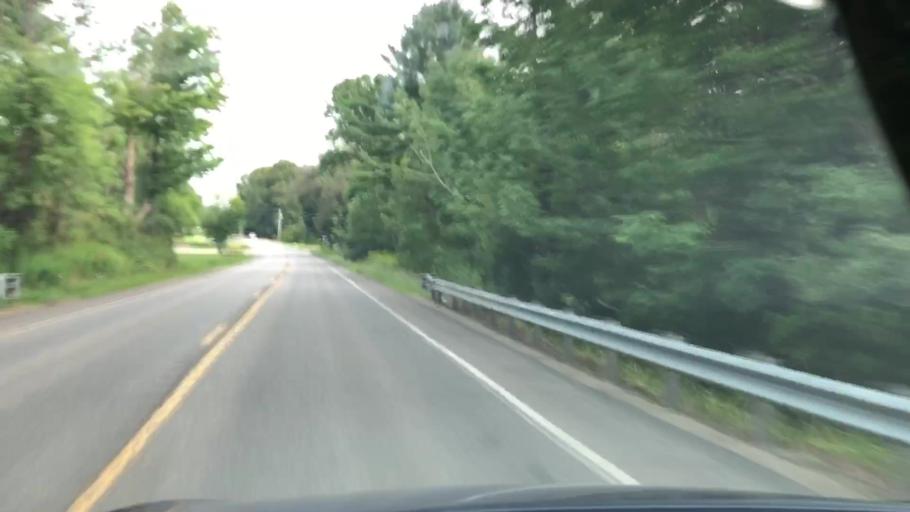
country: US
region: Pennsylvania
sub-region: Erie County
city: Union City
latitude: 41.8354
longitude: -79.8188
